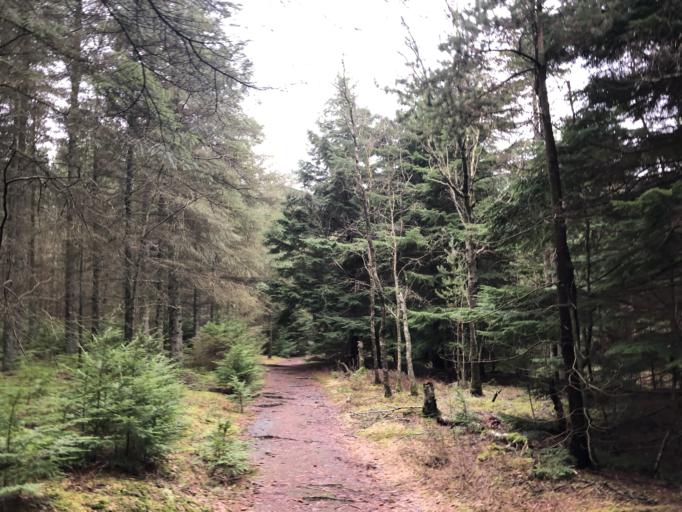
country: DK
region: Central Jutland
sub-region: Holstebro Kommune
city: Ulfborg
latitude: 56.2889
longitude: 8.1774
